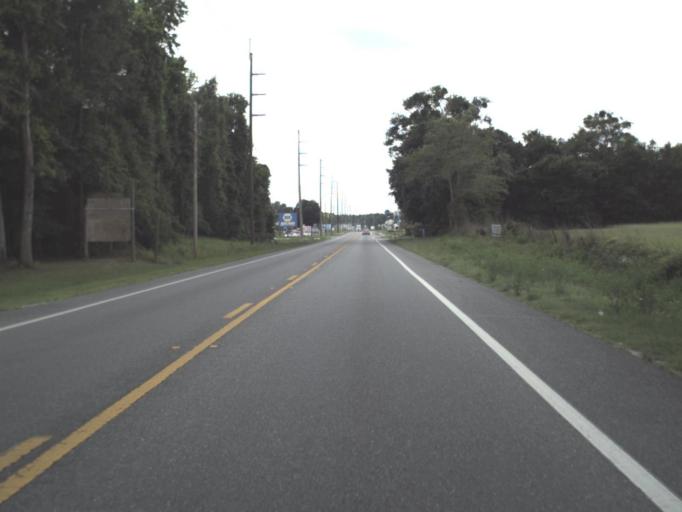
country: US
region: Florida
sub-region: Gilchrist County
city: Trenton
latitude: 29.6152
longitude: -82.7967
